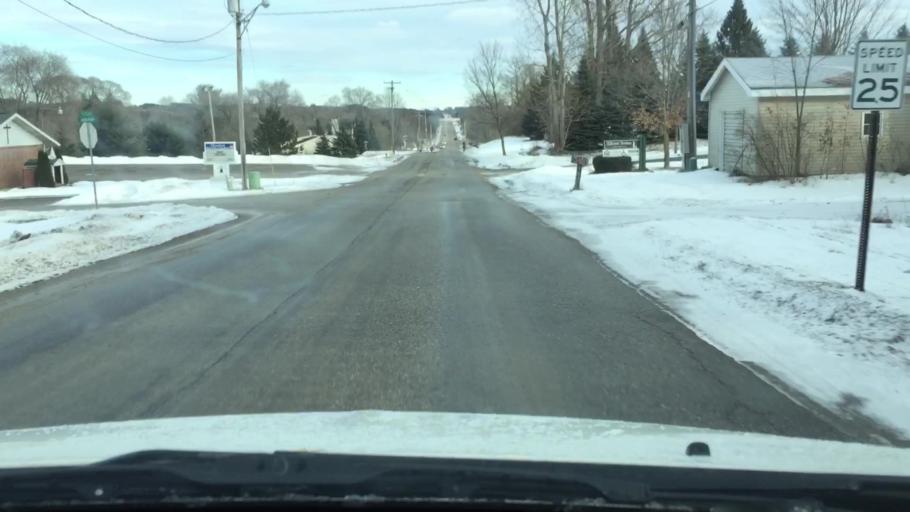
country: US
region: Michigan
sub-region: Wexford County
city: Manton
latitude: 44.4036
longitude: -85.4035
